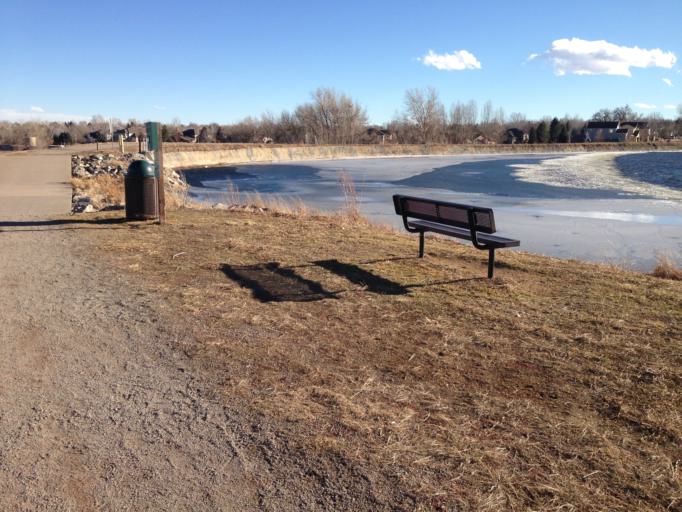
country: US
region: Colorado
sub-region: Boulder County
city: Lafayette
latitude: 40.0196
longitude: -105.0971
